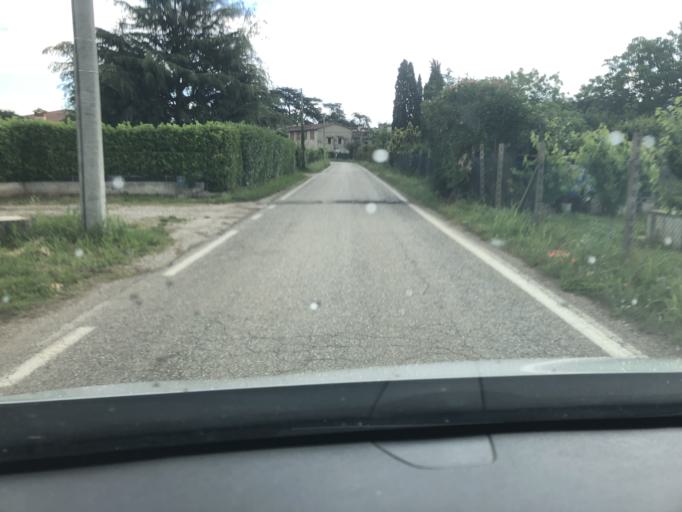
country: IT
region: Veneto
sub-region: Provincia di Verona
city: Sona
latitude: 45.4286
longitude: 10.8512
